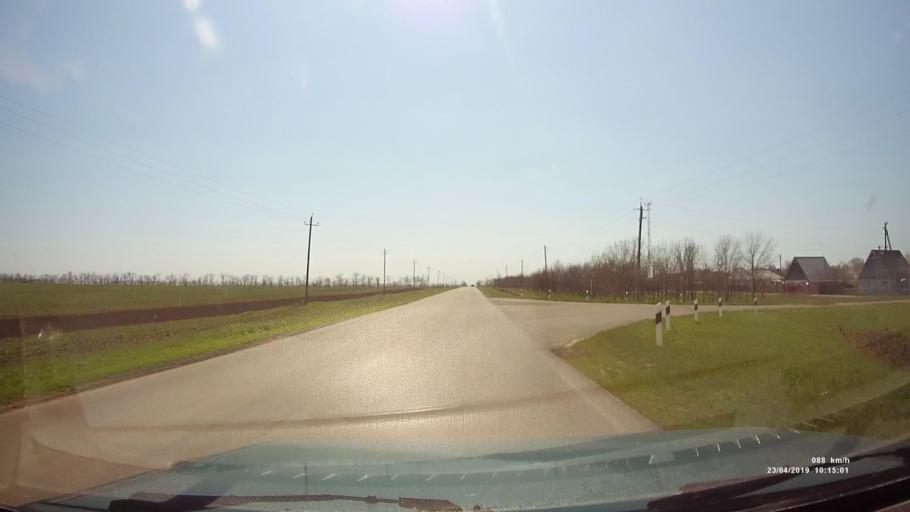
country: RU
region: Rostov
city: Sovetskoye
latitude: 46.6713
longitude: 42.3766
